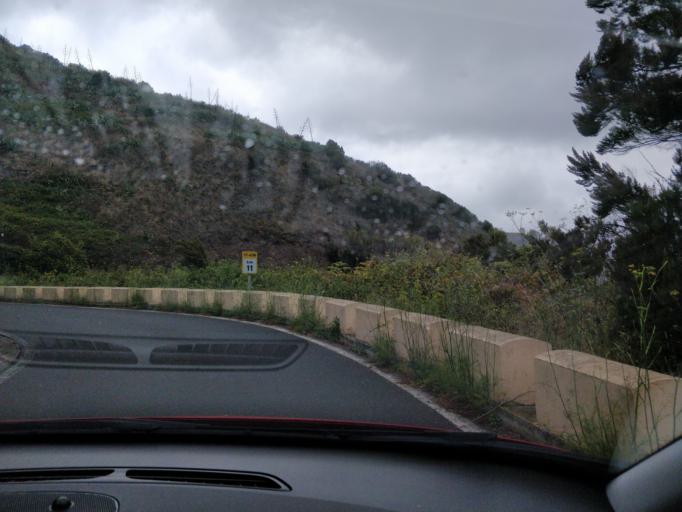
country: ES
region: Canary Islands
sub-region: Provincia de Santa Cruz de Tenerife
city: Santiago del Teide
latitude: 28.3230
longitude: -16.8499
